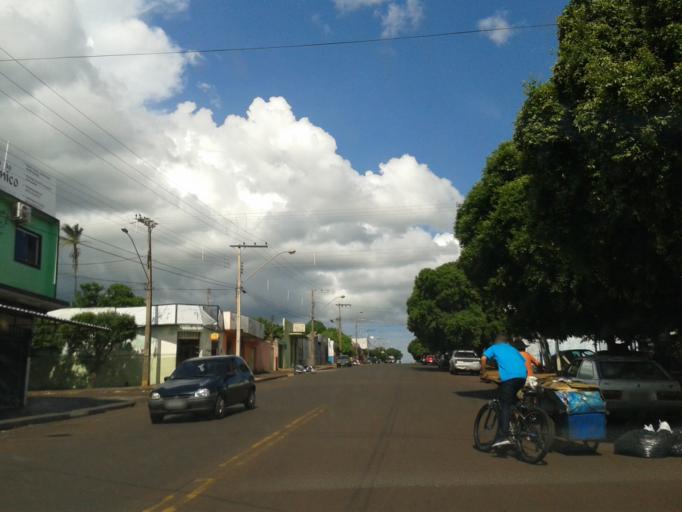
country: BR
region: Minas Gerais
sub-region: Ituiutaba
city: Ituiutaba
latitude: -18.9851
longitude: -49.4735
